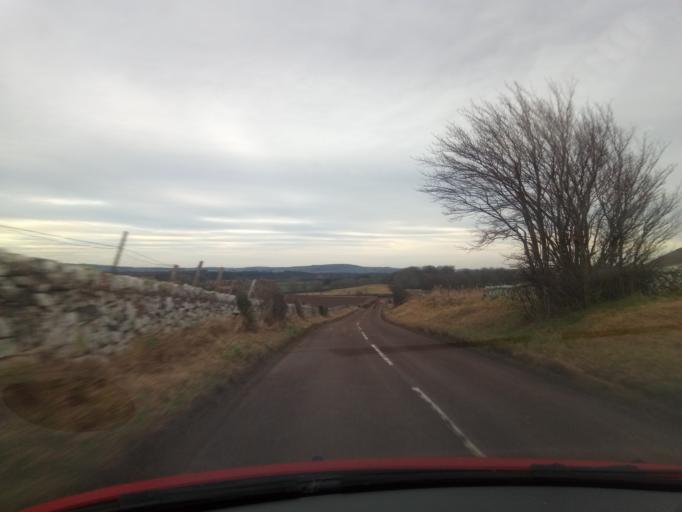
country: GB
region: England
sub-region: Northumberland
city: Kirknewton
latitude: 55.5682
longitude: -2.1159
